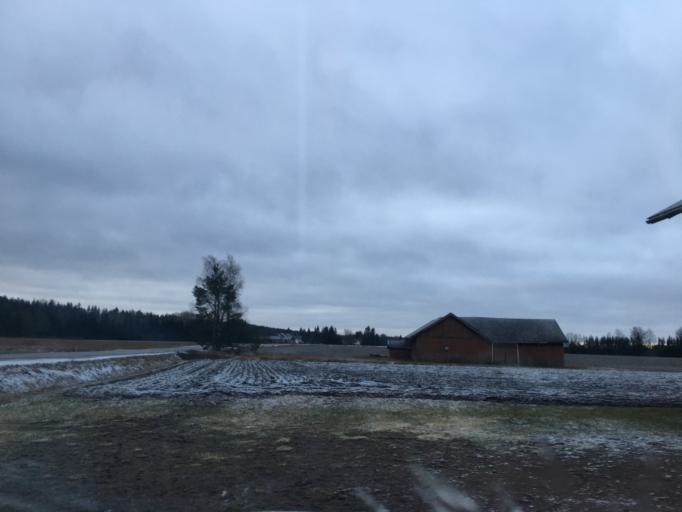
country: FI
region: Varsinais-Suomi
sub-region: Loimaa
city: Aura
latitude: 60.6235
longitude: 22.5819
